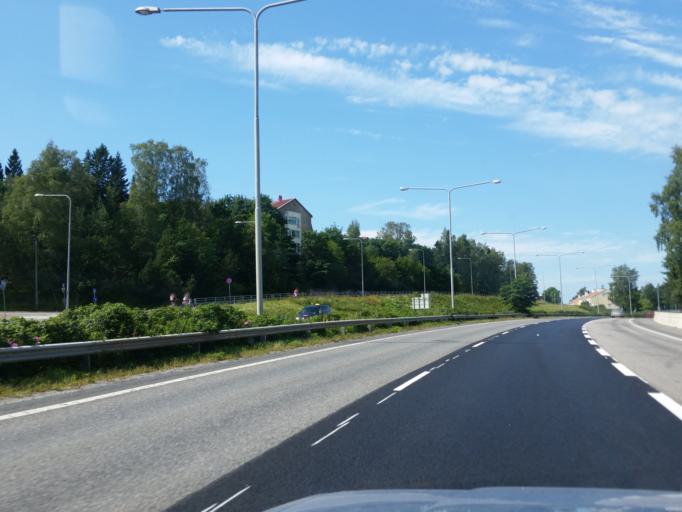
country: FI
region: Uusimaa
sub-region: Helsinki
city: Teekkarikylae
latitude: 60.1624
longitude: 24.8665
